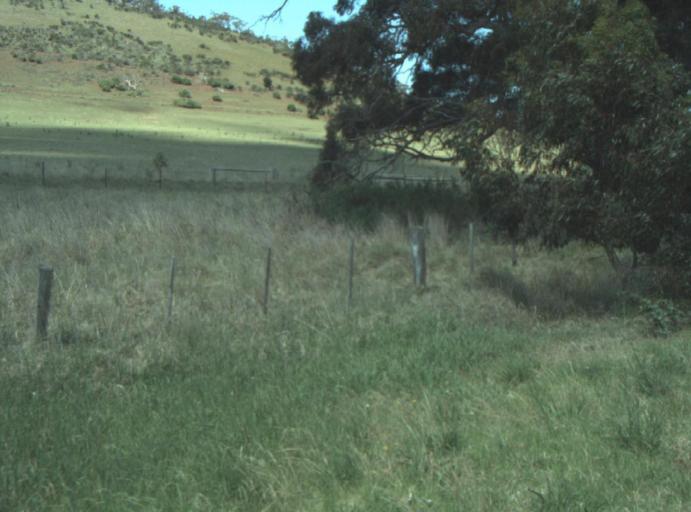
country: AU
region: Victoria
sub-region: Greater Geelong
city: Lara
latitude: -37.8792
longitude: 144.2652
